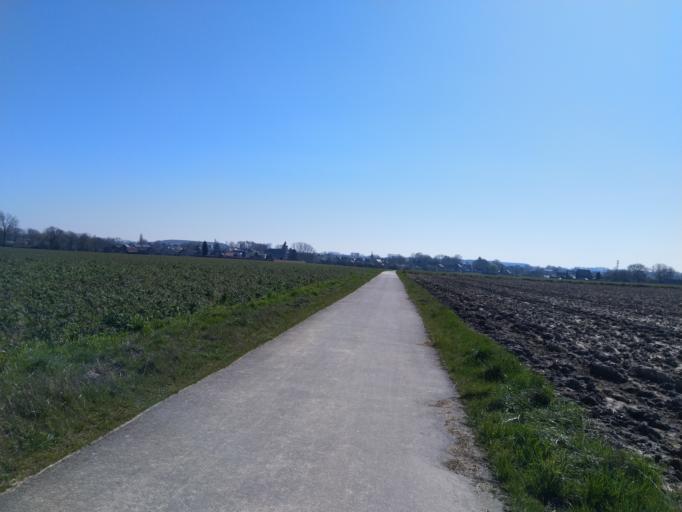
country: BE
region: Wallonia
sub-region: Province du Hainaut
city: Soignies
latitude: 50.5718
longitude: 3.9915
